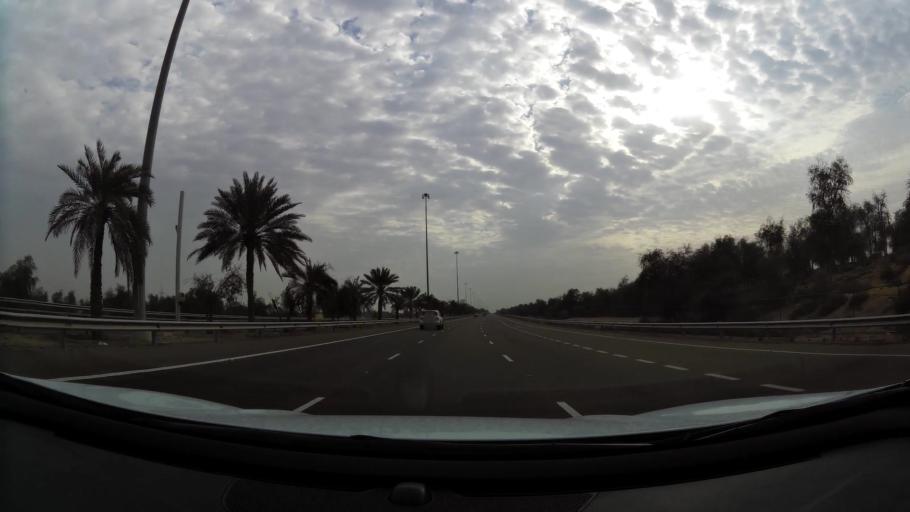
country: AE
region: Abu Dhabi
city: Al Ain
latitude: 24.1789
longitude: 55.1406
